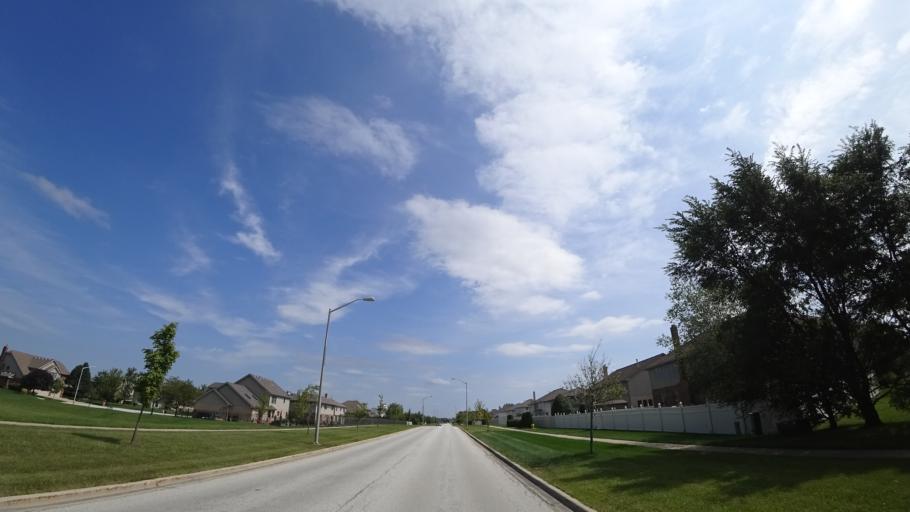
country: US
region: Illinois
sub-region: Cook County
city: Orland Hills
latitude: 41.5653
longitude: -87.8298
